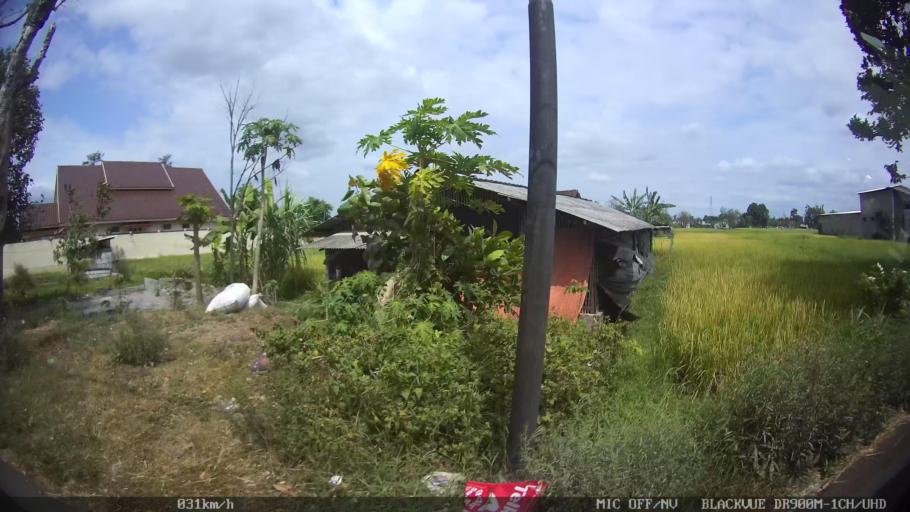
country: ID
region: Central Java
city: Candi Prambanan
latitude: -7.7893
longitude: 110.4822
